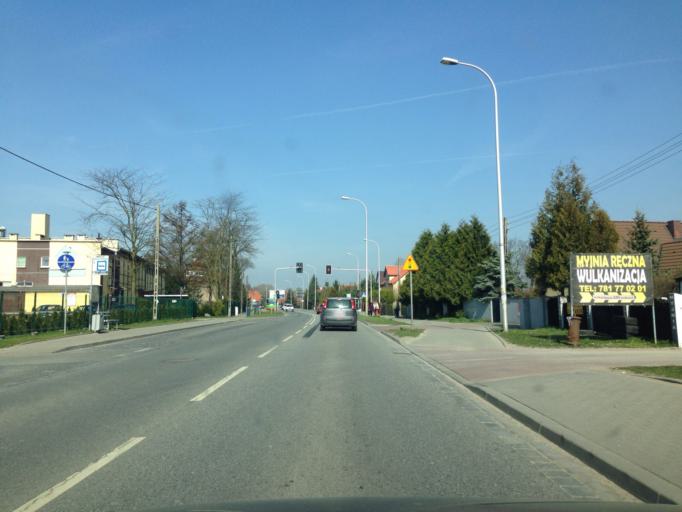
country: PL
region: Lower Silesian Voivodeship
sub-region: Powiat wroclawski
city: Wilczyce
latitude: 51.1026
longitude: 17.1559
